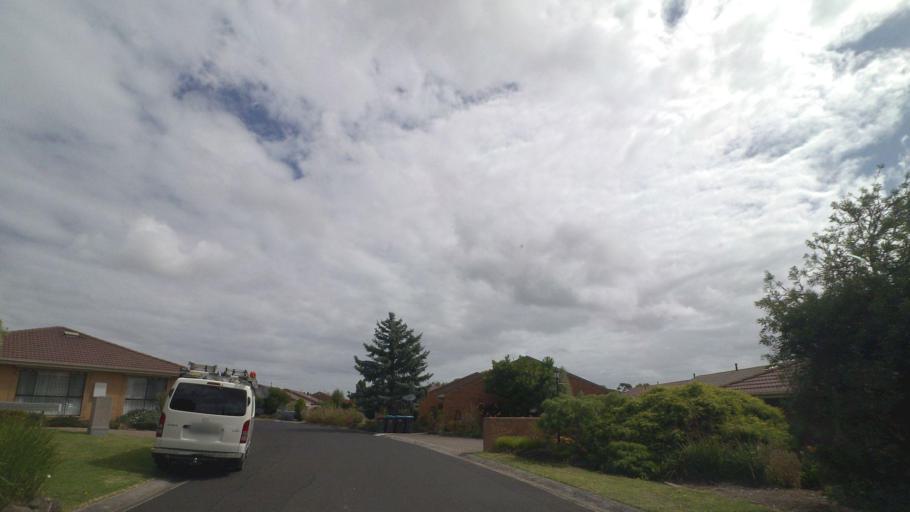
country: AU
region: Victoria
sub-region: Knox
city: Wantirna South
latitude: -37.8863
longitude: 145.2293
